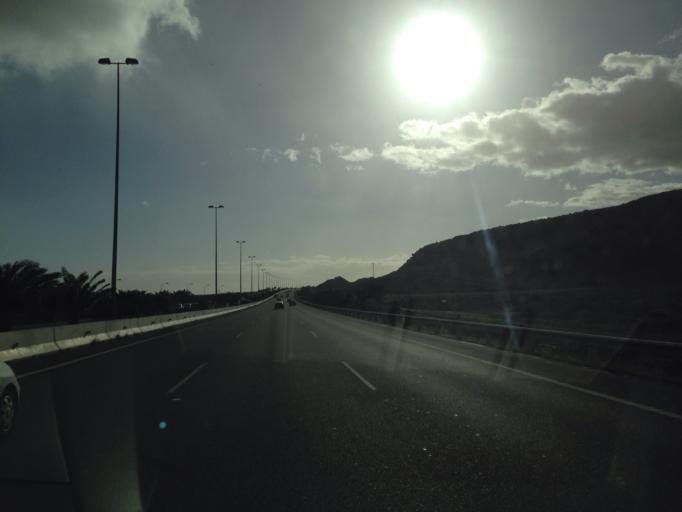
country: ES
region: Canary Islands
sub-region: Provincia de Las Palmas
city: Cruce de Arinaga
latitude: 27.8052
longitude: -15.4824
